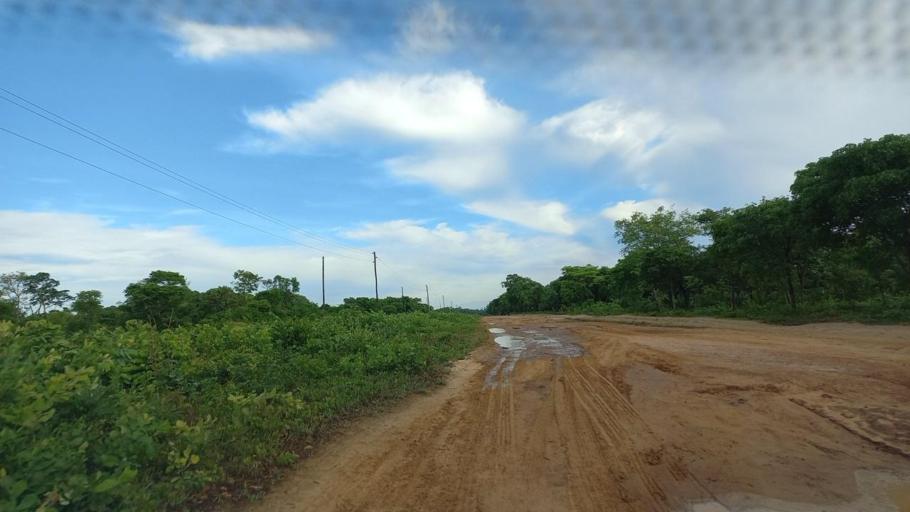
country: ZM
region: North-Western
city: Kabompo
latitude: -13.4113
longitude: 24.3160
